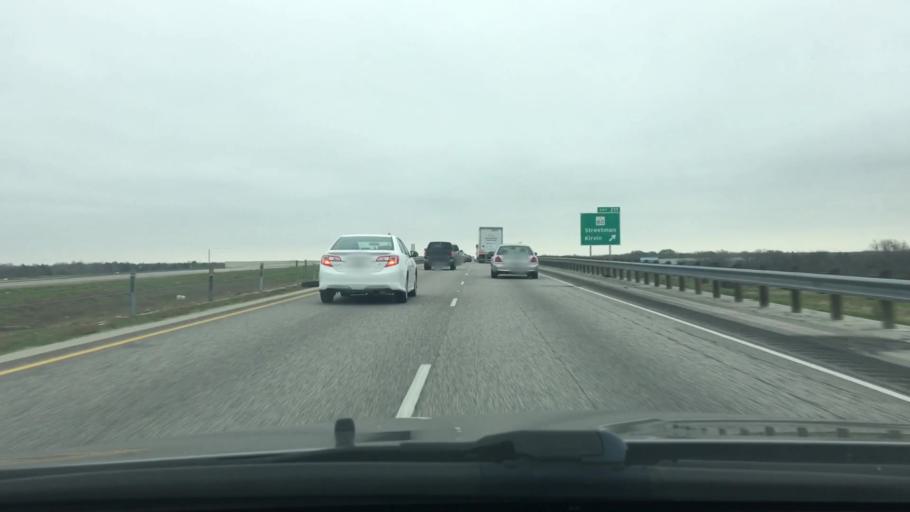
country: US
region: Texas
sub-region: Freestone County
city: Wortham
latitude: 31.8655
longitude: -96.3240
